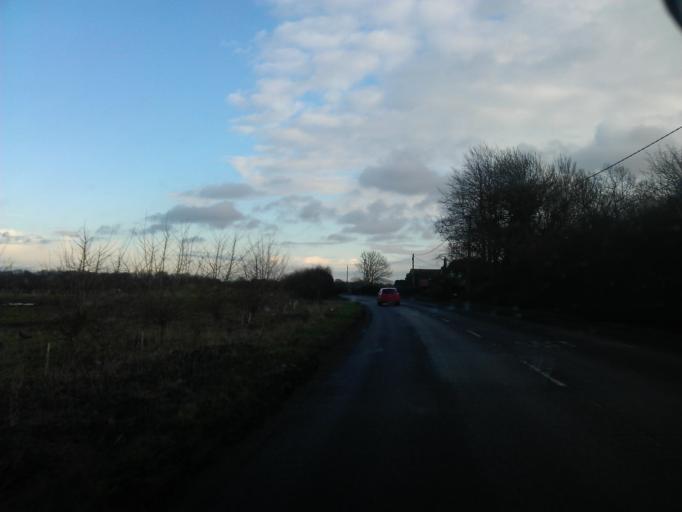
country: GB
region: England
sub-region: Essex
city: Alresford
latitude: 51.8805
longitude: 1.0024
